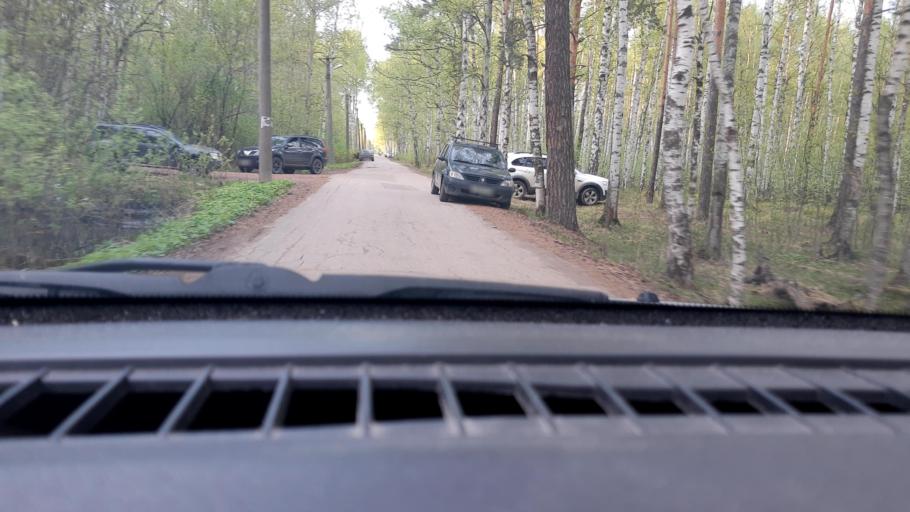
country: RU
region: Nizjnij Novgorod
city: Gorbatovka
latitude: 56.2850
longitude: 43.8294
